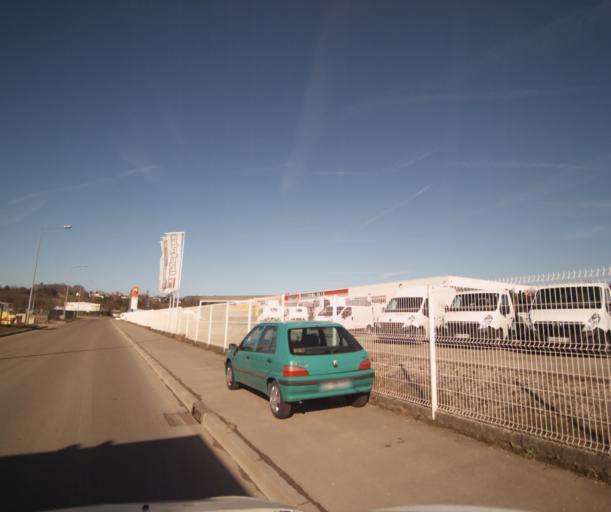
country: FR
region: Franche-Comte
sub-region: Departement du Doubs
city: Avanne-Aveney
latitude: 47.2280
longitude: 5.9740
